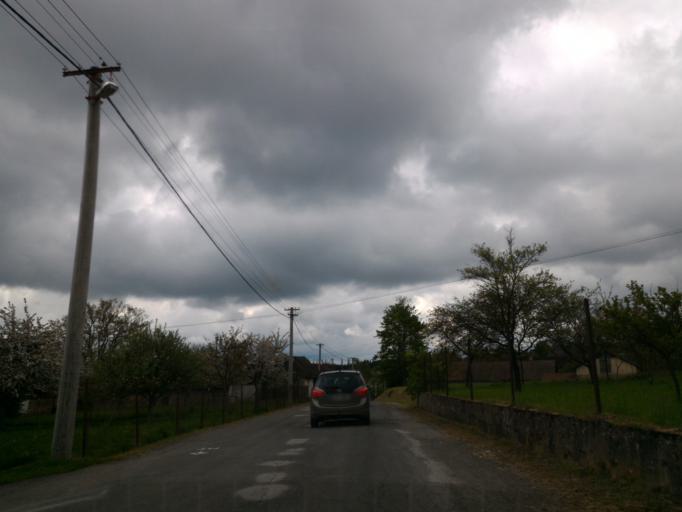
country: CZ
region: Vysocina
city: Ledec nad Sazavou
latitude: 49.6302
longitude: 15.2927
